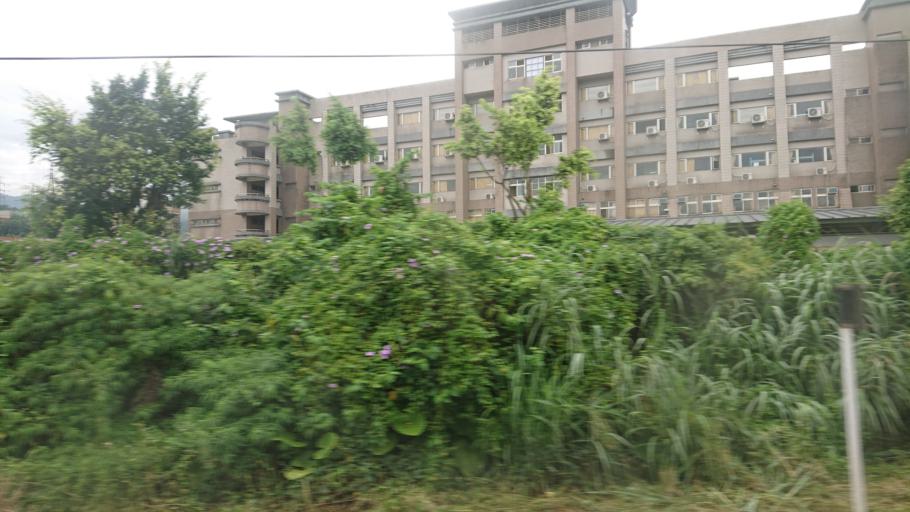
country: TW
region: Taiwan
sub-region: Keelung
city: Keelung
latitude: 25.0788
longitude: 121.6885
